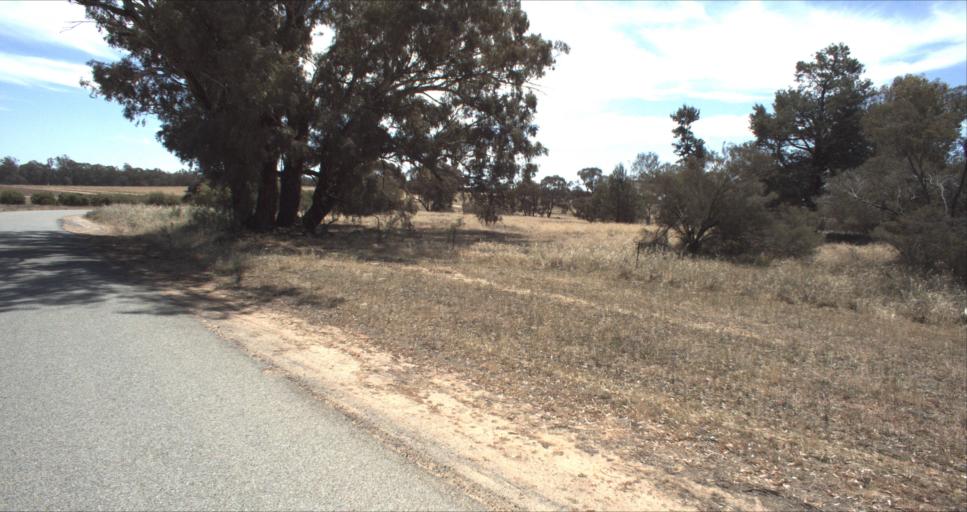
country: AU
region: New South Wales
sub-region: Leeton
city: Leeton
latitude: -34.6760
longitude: 146.4338
